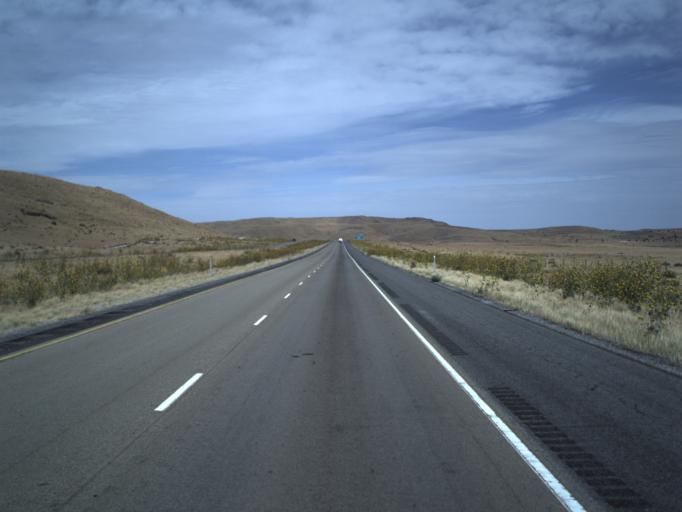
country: US
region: Utah
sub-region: Tooele County
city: Grantsville
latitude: 40.8147
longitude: -112.8759
